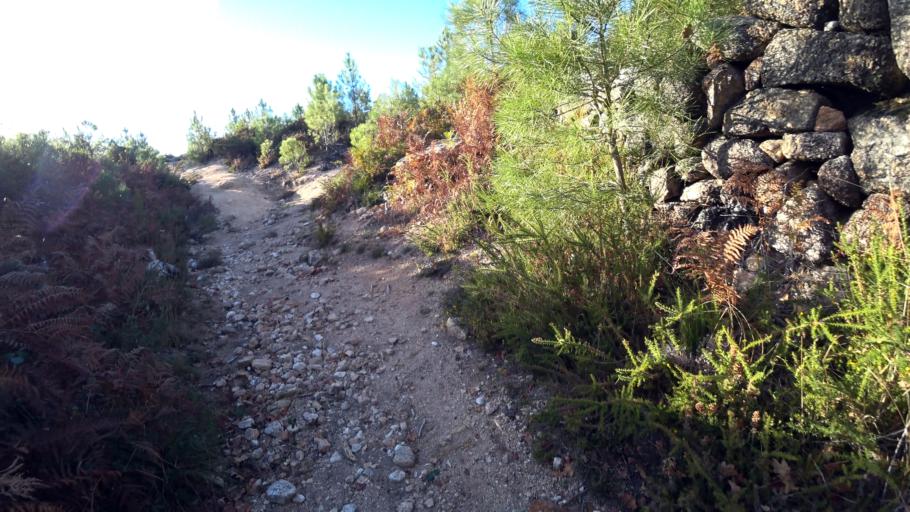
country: PT
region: Braga
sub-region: Terras de Bouro
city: Antas
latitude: 41.7717
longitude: -8.1885
